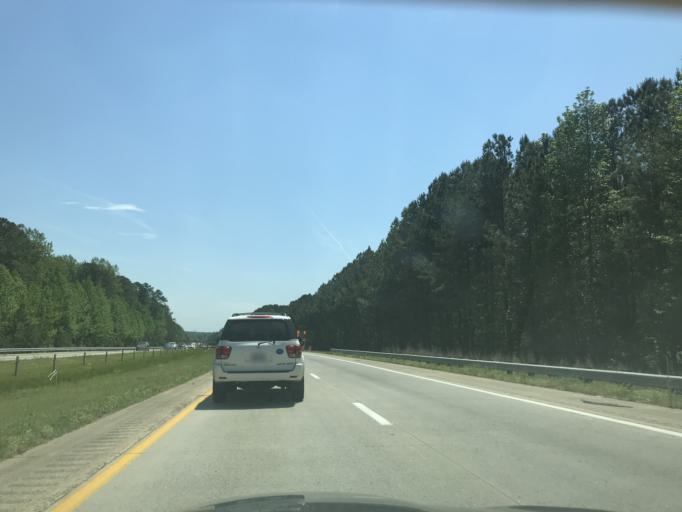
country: US
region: North Carolina
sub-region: Wake County
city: Garner
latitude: 35.5805
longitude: -78.5765
